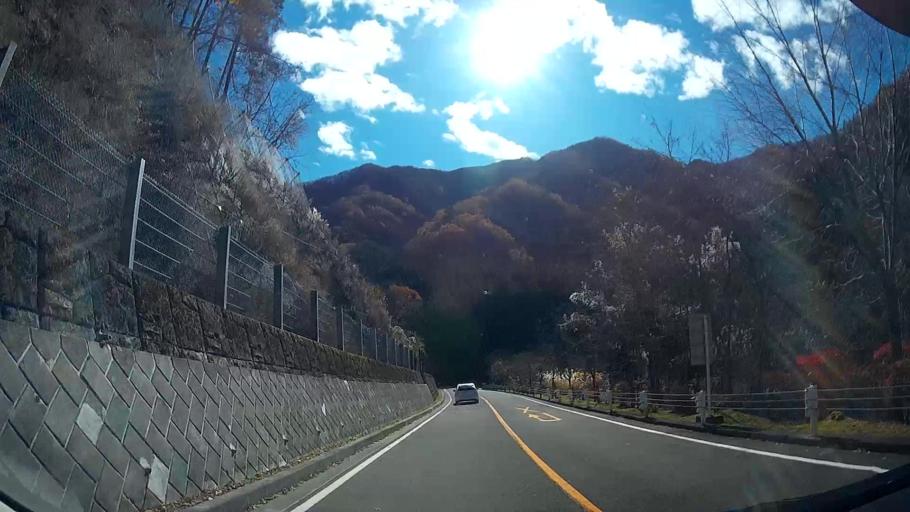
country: JP
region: Yamanashi
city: Uenohara
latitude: 35.7556
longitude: 139.0278
